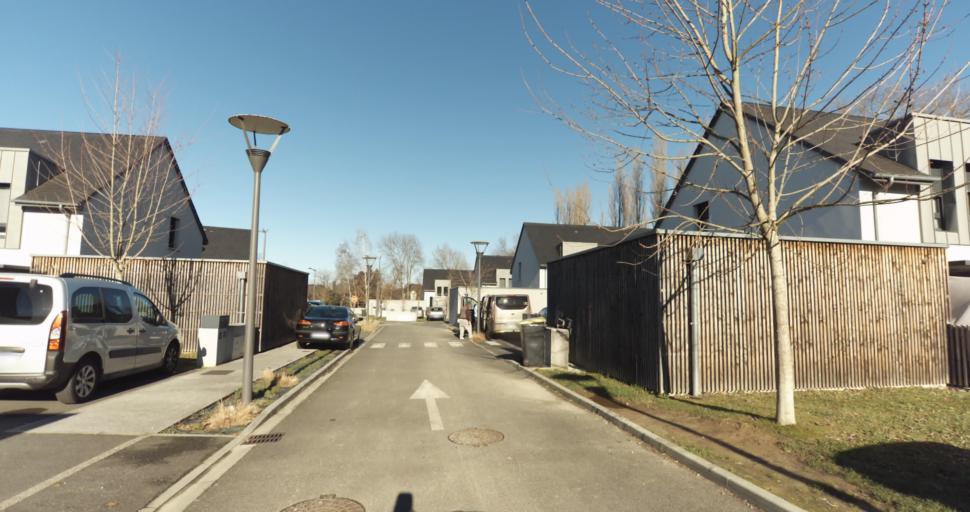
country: FR
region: Aquitaine
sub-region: Departement des Pyrenees-Atlantiques
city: Morlaas
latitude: 43.3437
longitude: -0.2560
